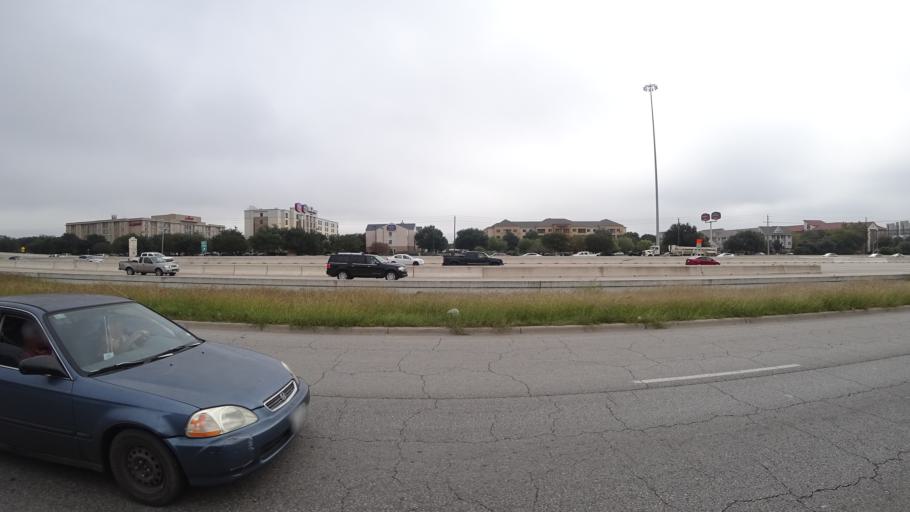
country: US
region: Texas
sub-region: Travis County
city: Austin
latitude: 30.2104
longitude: -97.7557
